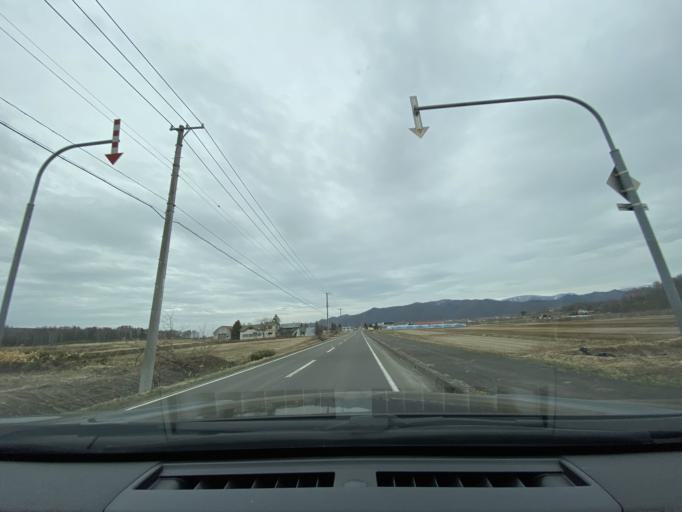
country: JP
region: Hokkaido
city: Nayoro
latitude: 44.1047
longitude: 142.4770
